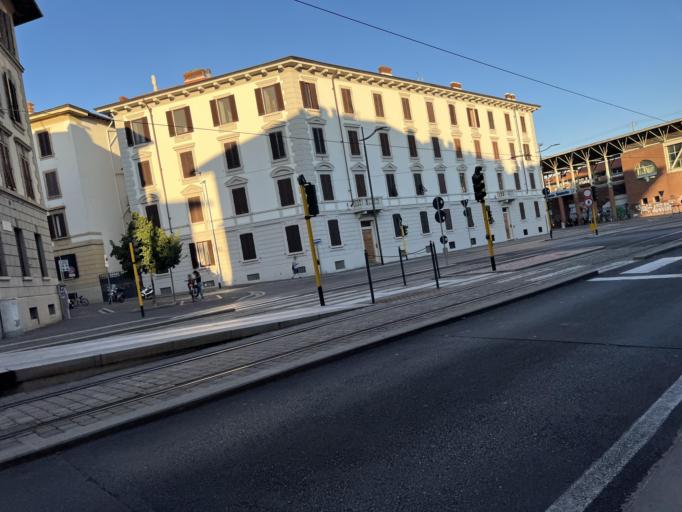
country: IT
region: Tuscany
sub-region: Province of Florence
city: Florence
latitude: 43.7881
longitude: 11.2494
